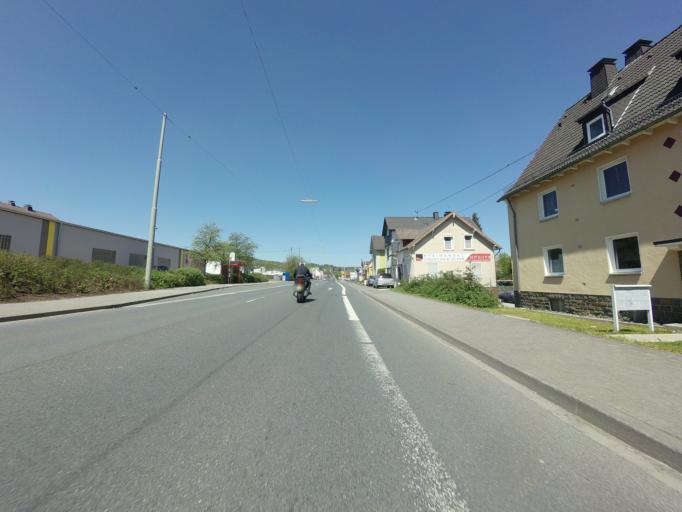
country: DE
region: North Rhine-Westphalia
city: Kreuztal
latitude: 50.9830
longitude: 7.9638
